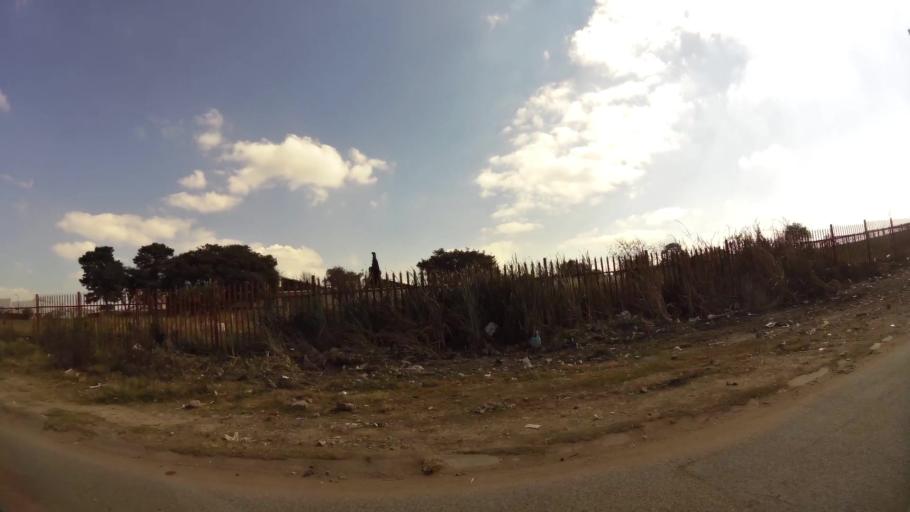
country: ZA
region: Gauteng
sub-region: Ekurhuleni Metropolitan Municipality
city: Tembisa
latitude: -26.0262
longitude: 28.1877
